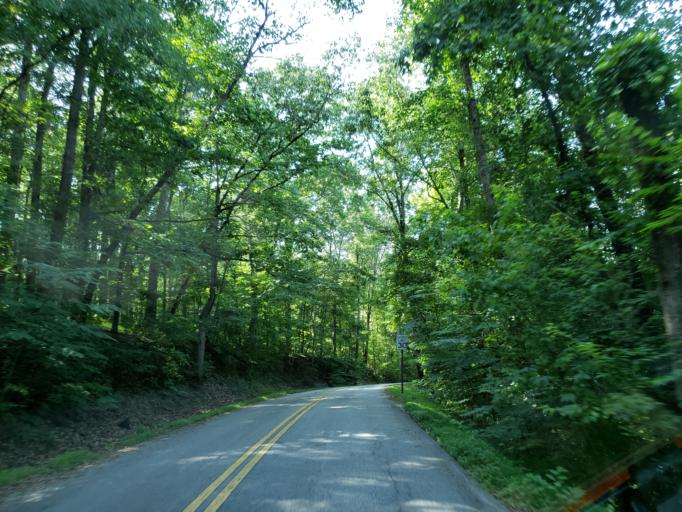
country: US
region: Georgia
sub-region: Cobb County
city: Mableton
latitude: 33.8498
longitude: -84.5597
